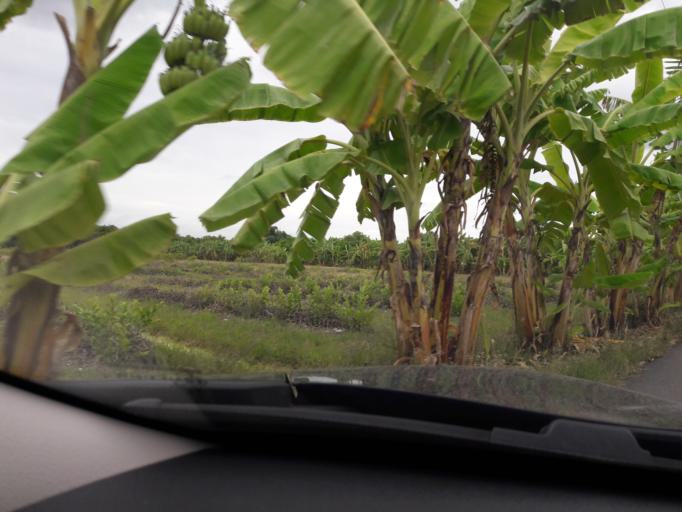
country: TH
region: Ratchaburi
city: Bang Phae
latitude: 13.6269
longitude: 99.9556
